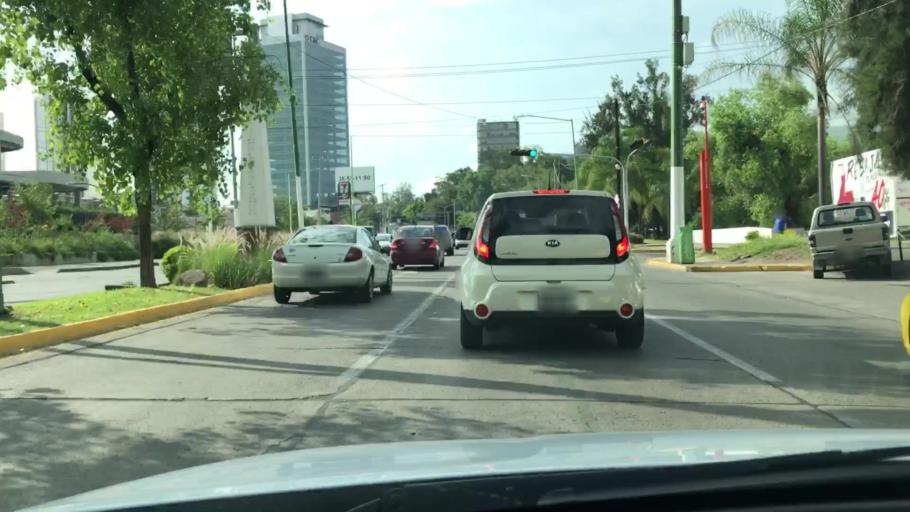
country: MX
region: Jalisco
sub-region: Zapopan
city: Zapopan
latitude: 20.7123
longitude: -103.3812
